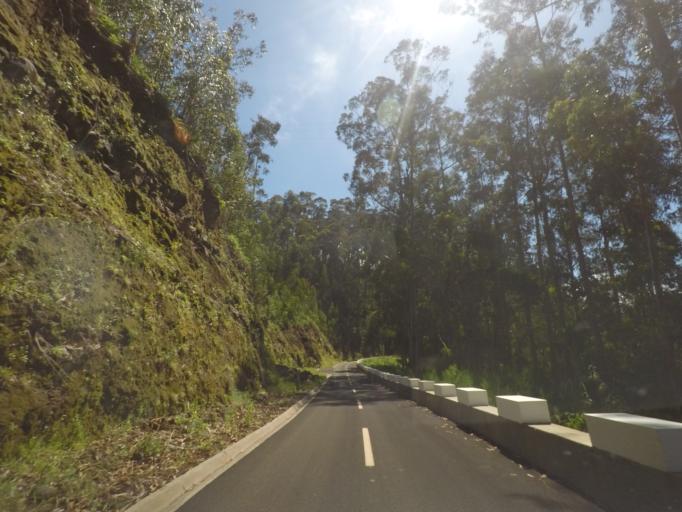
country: PT
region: Madeira
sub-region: Calheta
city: Arco da Calheta
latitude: 32.7275
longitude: -17.1210
